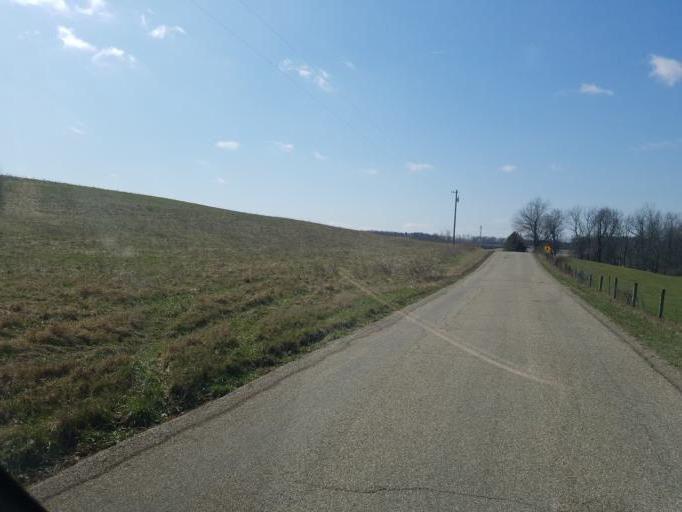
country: US
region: Ohio
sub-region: Licking County
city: Utica
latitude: 40.2489
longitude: -82.3376
